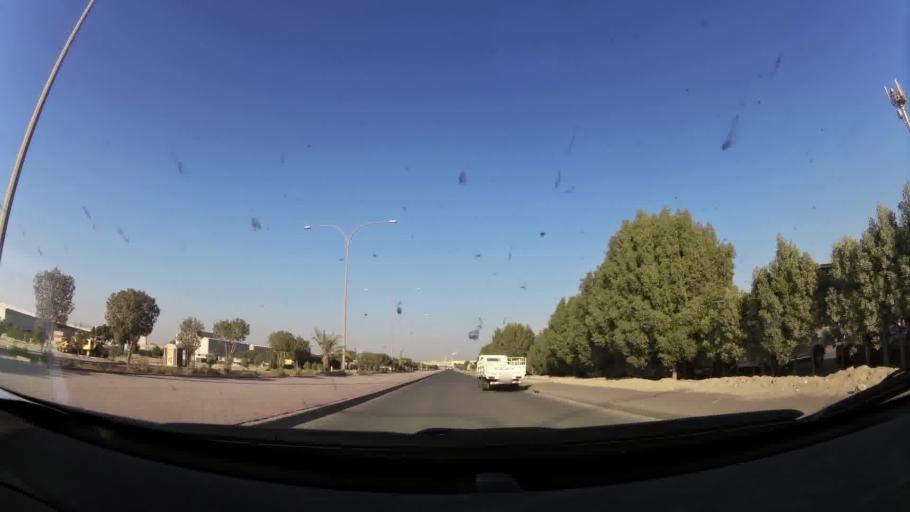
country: KW
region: Al Ahmadi
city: Al Fahahil
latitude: 29.0044
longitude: 48.1272
